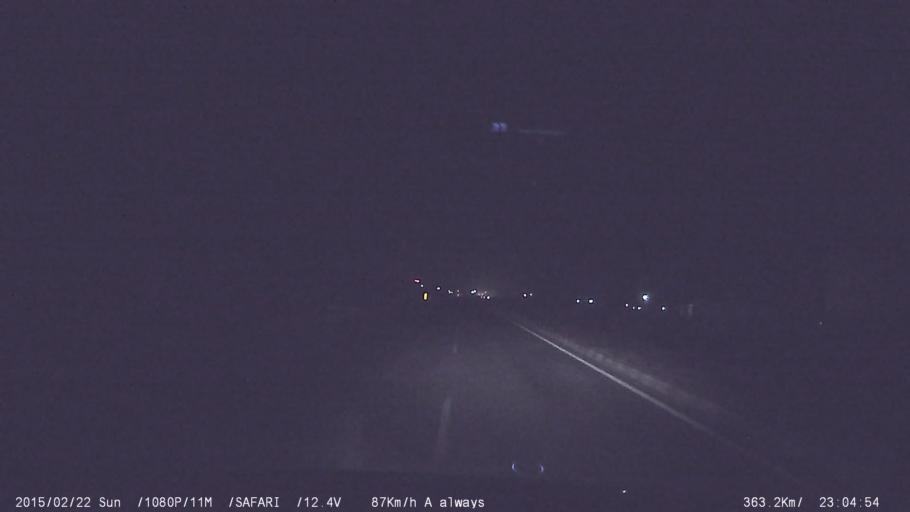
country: IN
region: Tamil Nadu
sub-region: Namakkal
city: Rasipuram
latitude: 11.4082
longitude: 78.1591
